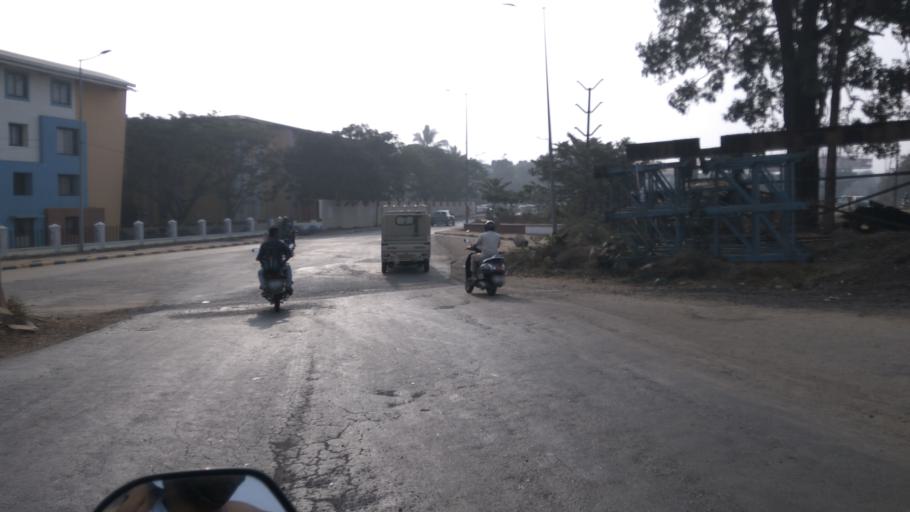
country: IN
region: Goa
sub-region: North Goa
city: Panaji
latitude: 15.5167
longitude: 73.8340
